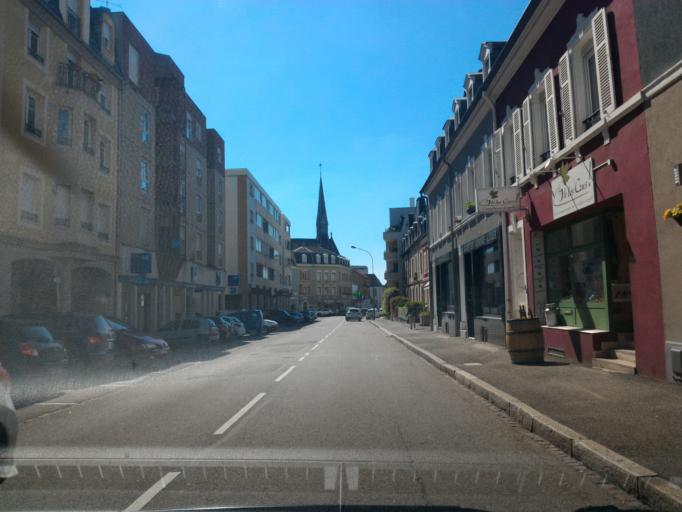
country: FR
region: Alsace
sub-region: Departement du Haut-Rhin
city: Riedisheim
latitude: 47.7465
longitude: 7.3600
